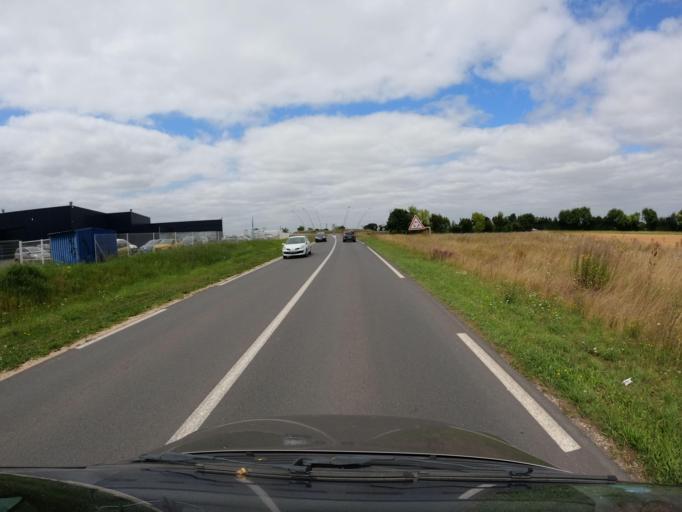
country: FR
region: Poitou-Charentes
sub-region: Departement de la Vienne
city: Civray
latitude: 46.1618
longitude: 0.3005
